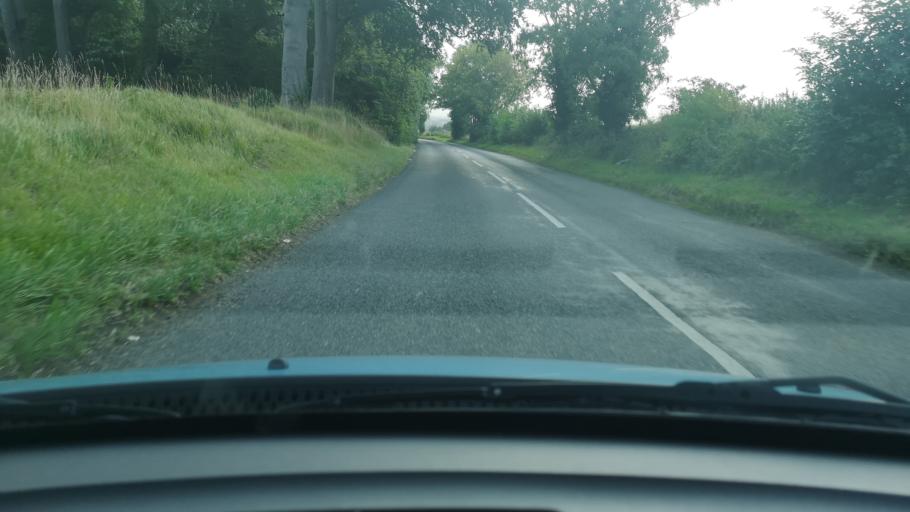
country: GB
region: England
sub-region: Doncaster
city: Campsall
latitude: 53.6176
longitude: -1.2053
